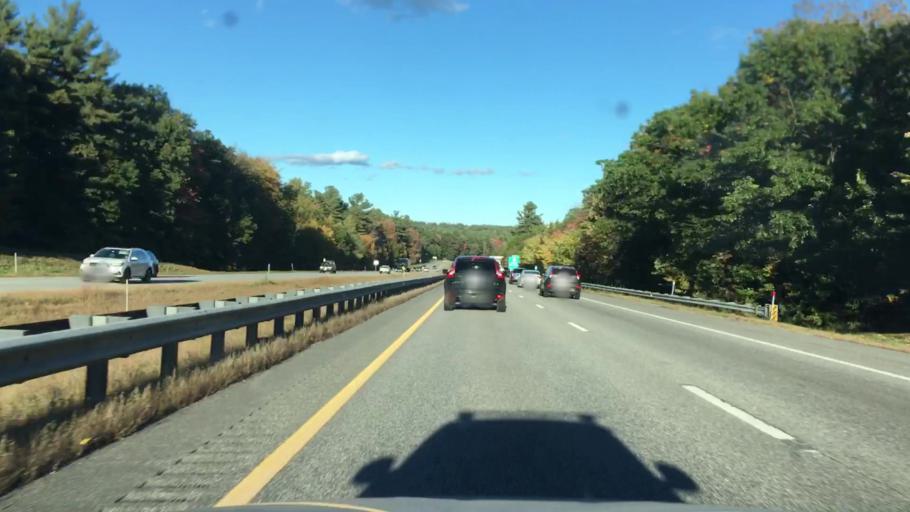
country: US
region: New Hampshire
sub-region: Rockingham County
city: Auburn
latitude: 43.0345
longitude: -71.3380
